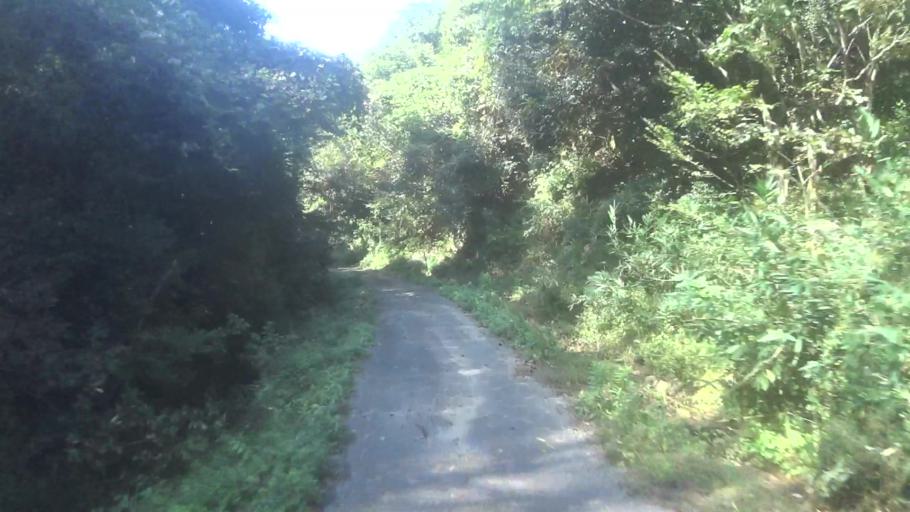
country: JP
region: Kyoto
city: Miyazu
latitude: 35.6997
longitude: 135.1250
